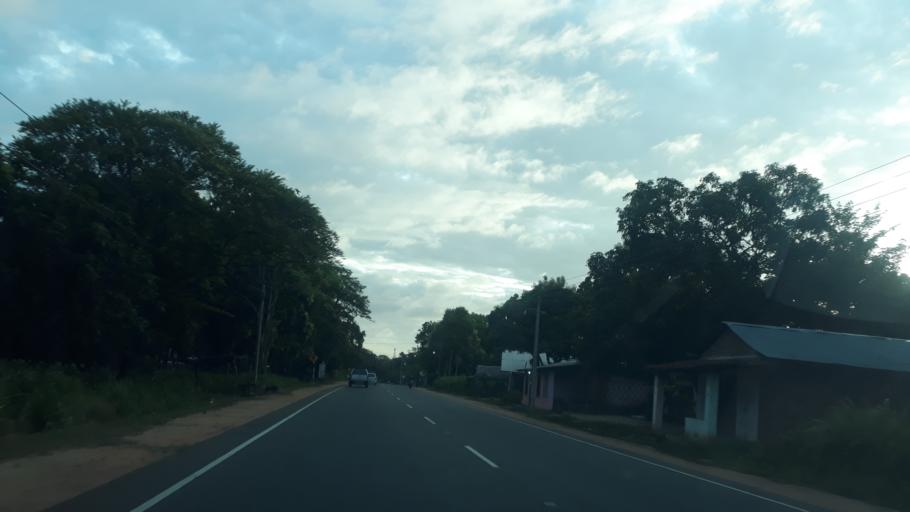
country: LK
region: Central
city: Sigiriya
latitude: 7.9763
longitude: 80.7152
